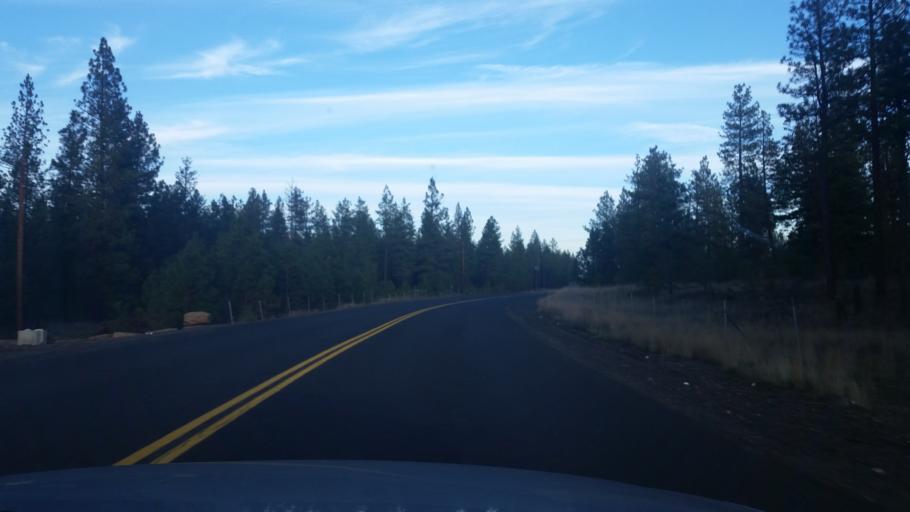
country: US
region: Washington
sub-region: Spokane County
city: Cheney
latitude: 47.4951
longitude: -117.4891
